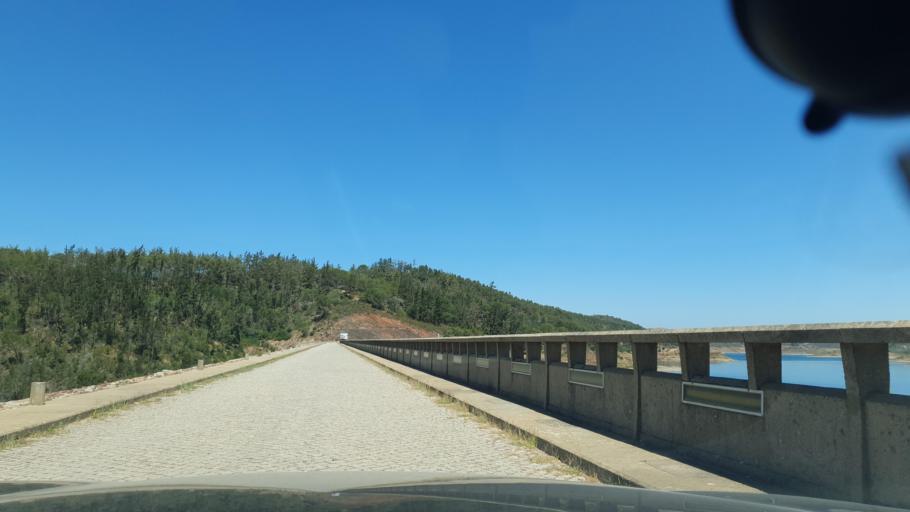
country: PT
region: Beja
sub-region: Odemira
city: Odemira
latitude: 37.5128
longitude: -8.4410
